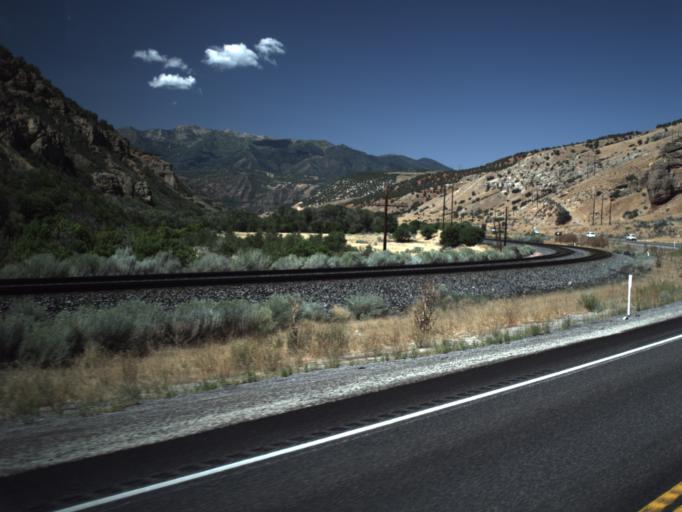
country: US
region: Utah
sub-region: Utah County
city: Mapleton
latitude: 39.9960
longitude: -111.4033
